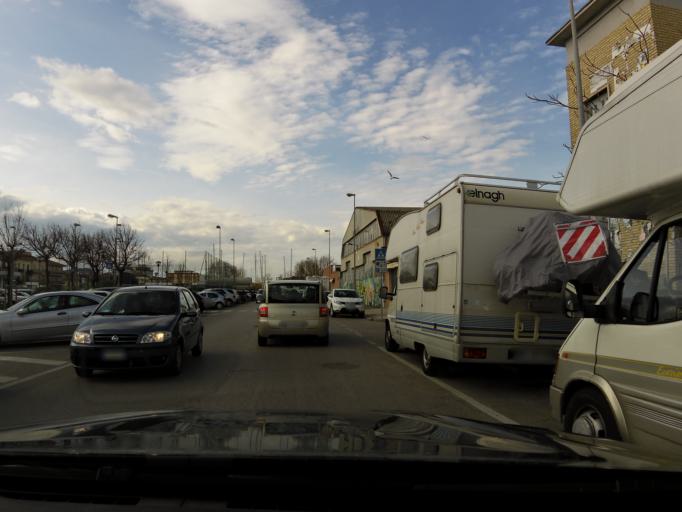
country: IT
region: The Marches
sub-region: Provincia di Macerata
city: Portocivitanova
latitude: 43.3108
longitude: 13.7293
